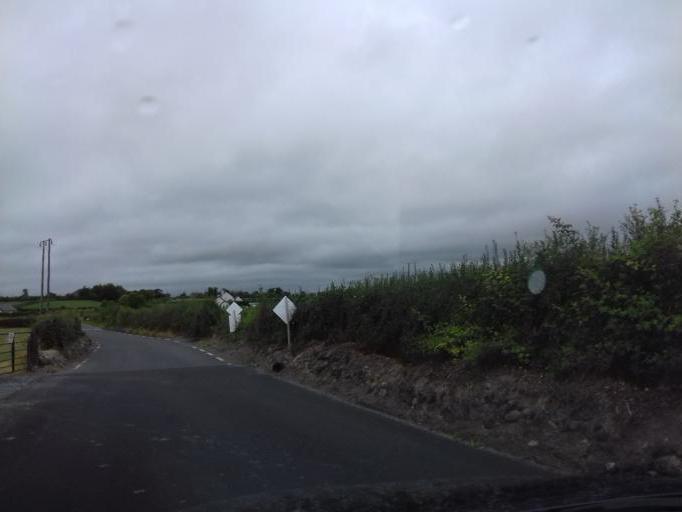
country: IE
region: Leinster
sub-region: Kilkenny
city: Graiguenamanagh
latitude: 52.6094
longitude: -7.0273
